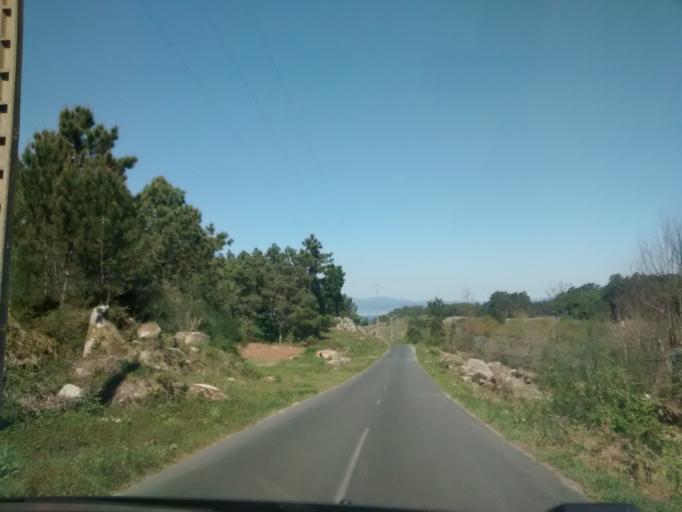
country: ES
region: Galicia
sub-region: Provincia de Pontevedra
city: O Grove
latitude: 42.4735
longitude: -8.8823
